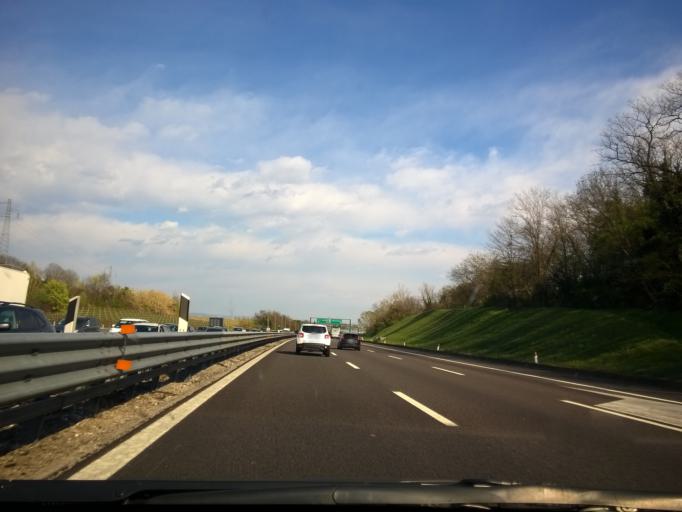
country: IT
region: Veneto
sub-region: Provincia di Verona
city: Sommacampagna
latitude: 45.4177
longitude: 10.8428
